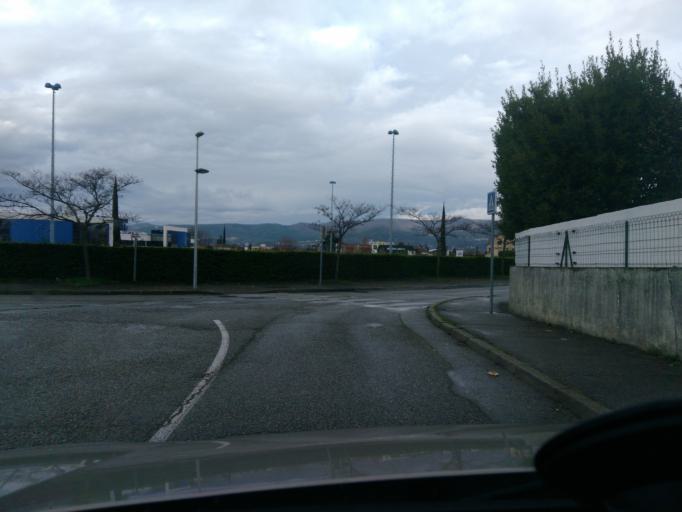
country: FR
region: Rhone-Alpes
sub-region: Departement de la Drome
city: Montelimar
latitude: 44.5674
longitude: 4.7587
